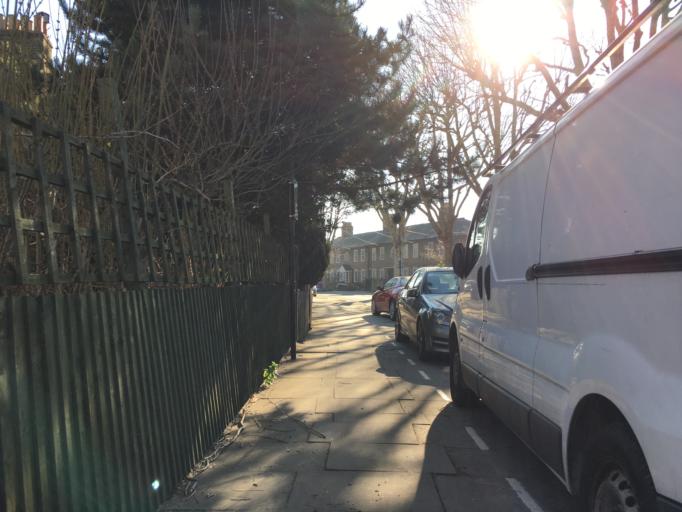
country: GB
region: England
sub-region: Greater London
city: Poplar
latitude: 51.4899
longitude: -0.0163
